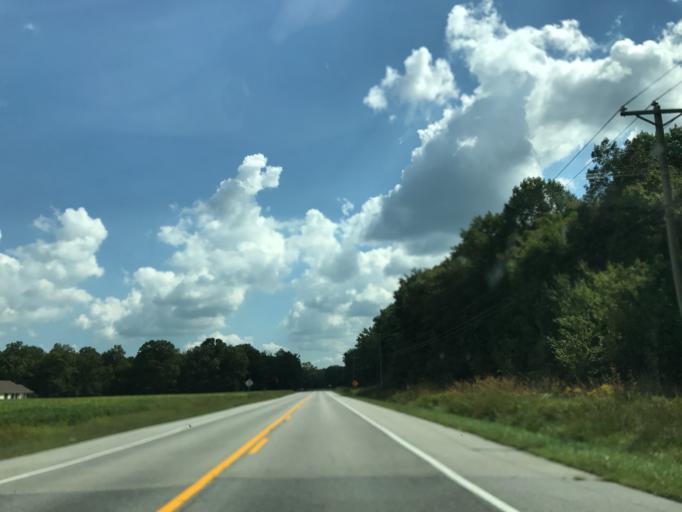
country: US
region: Maryland
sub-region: Caroline County
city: Greensboro
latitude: 39.1437
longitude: -75.8153
